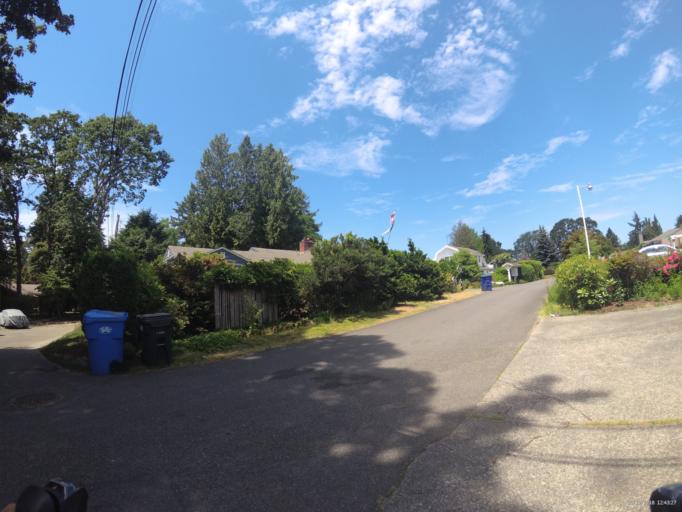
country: US
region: Washington
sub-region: Pierce County
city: Lakewood
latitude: 47.1626
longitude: -122.5239
